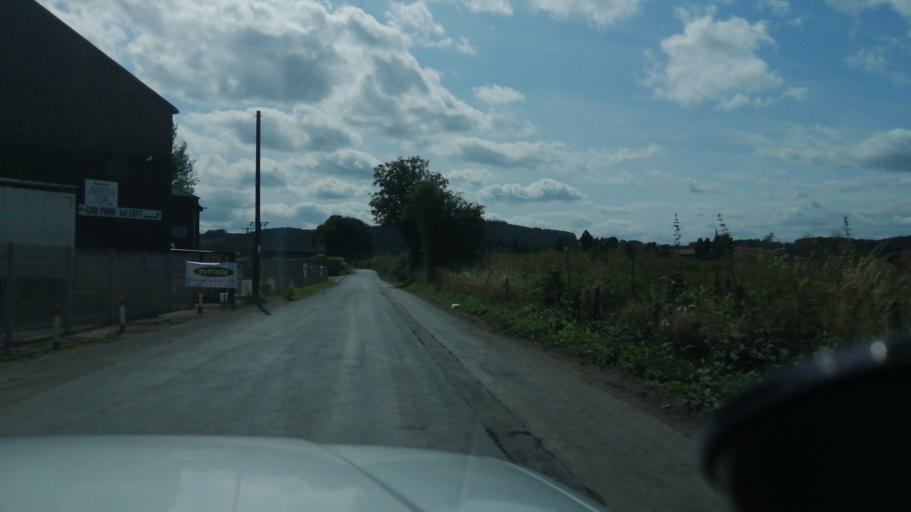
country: GB
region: England
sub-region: Herefordshire
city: Madley
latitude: 52.0295
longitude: -2.8538
